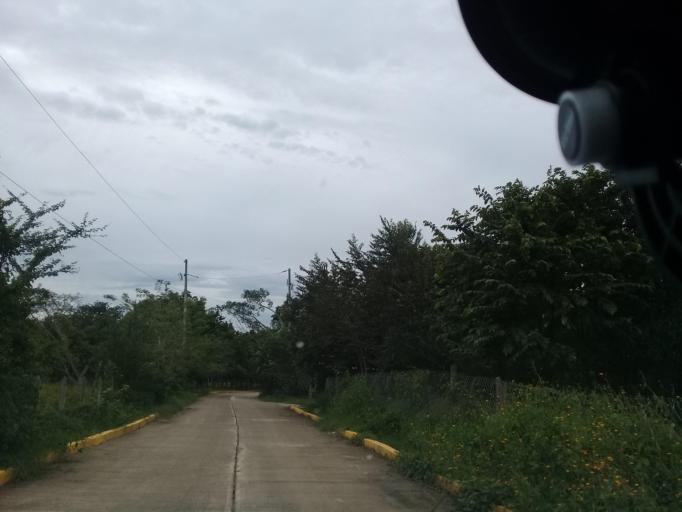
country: MX
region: Hidalgo
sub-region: Huejutla de Reyes
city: Chalahuiyapa
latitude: 21.1631
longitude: -98.3642
